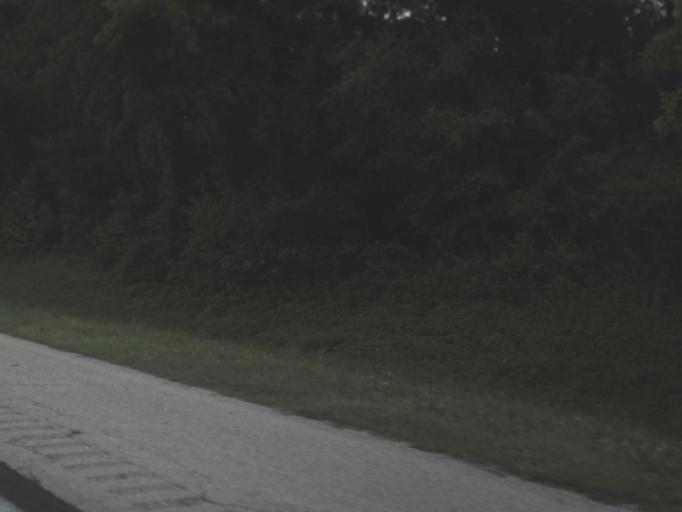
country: US
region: Florida
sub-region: Alachua County
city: Gainesville
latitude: 29.6347
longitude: -82.3982
